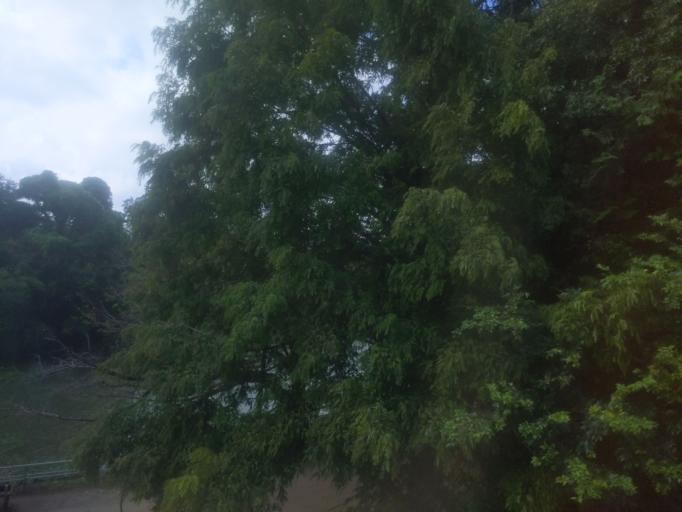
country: JP
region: Tokyo
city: Musashino
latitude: 35.7283
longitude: 139.5687
